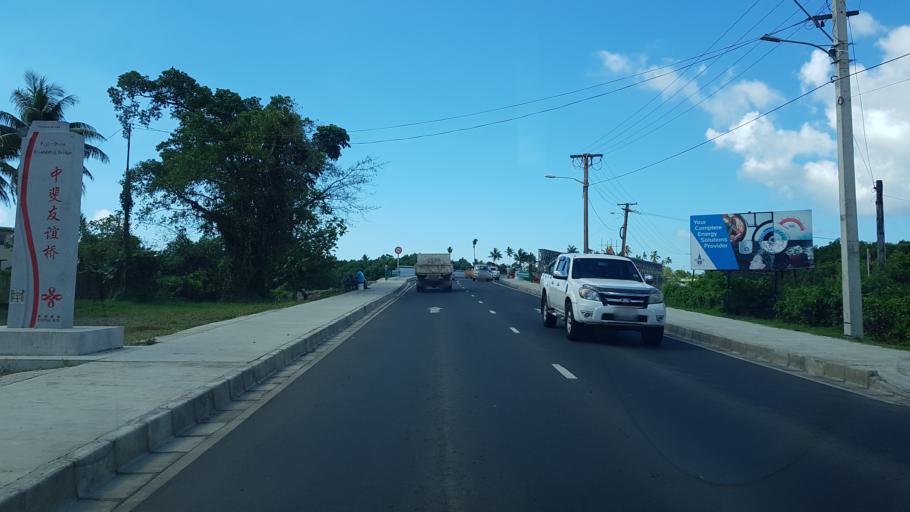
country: FJ
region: Central
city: Suva
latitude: -18.1375
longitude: 178.4586
